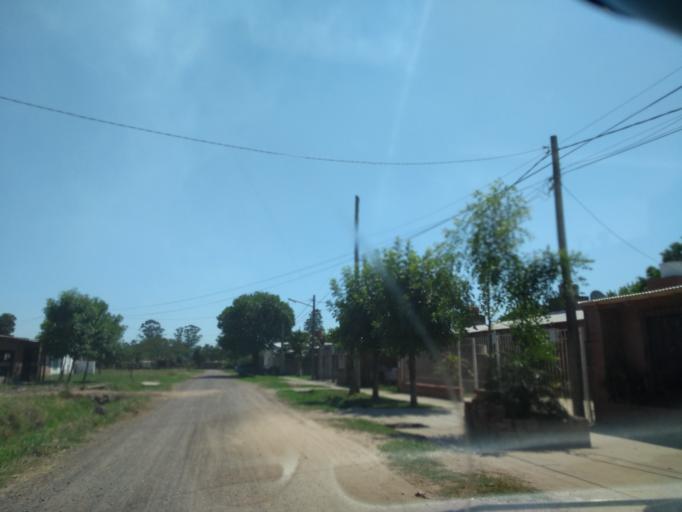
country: AR
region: Chaco
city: Fontana
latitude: -27.4143
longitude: -59.0403
